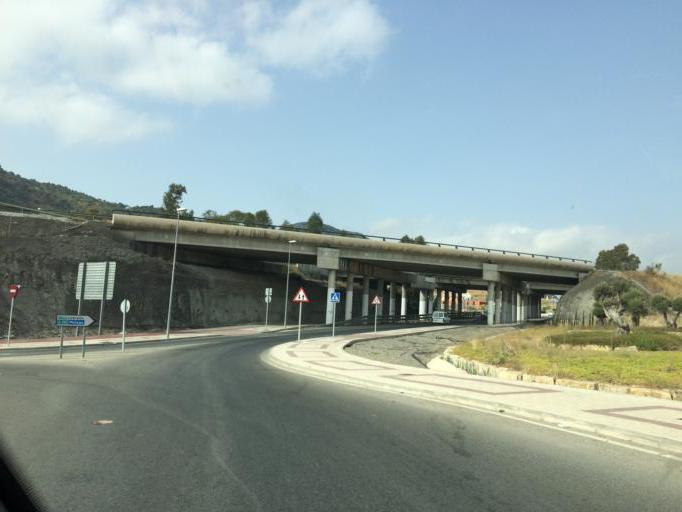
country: ES
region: Andalusia
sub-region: Provincia de Malaga
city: Cartama
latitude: 36.7186
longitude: -4.6207
